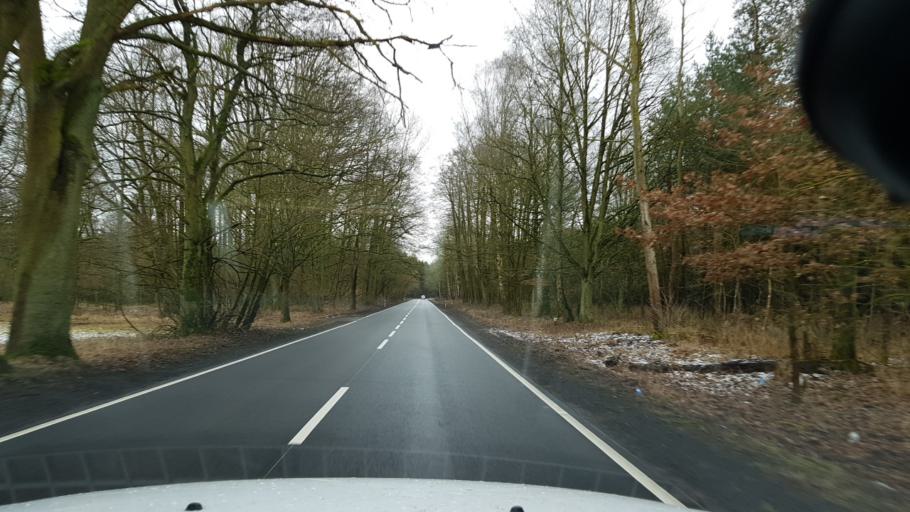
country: PL
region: West Pomeranian Voivodeship
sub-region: Powiat goleniowski
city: Stepnica
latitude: 53.6443
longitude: 14.6575
